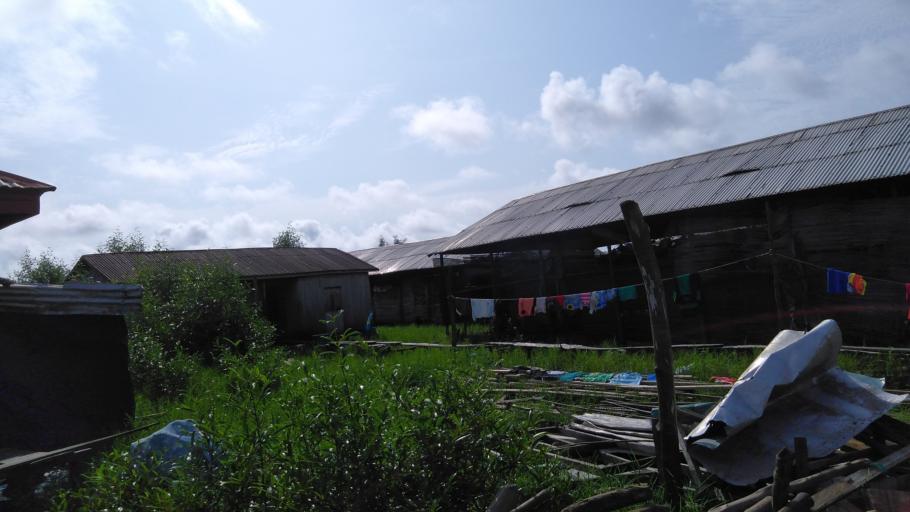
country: NG
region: Ondo
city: Igbekebo
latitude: 5.9285
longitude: 4.9607
